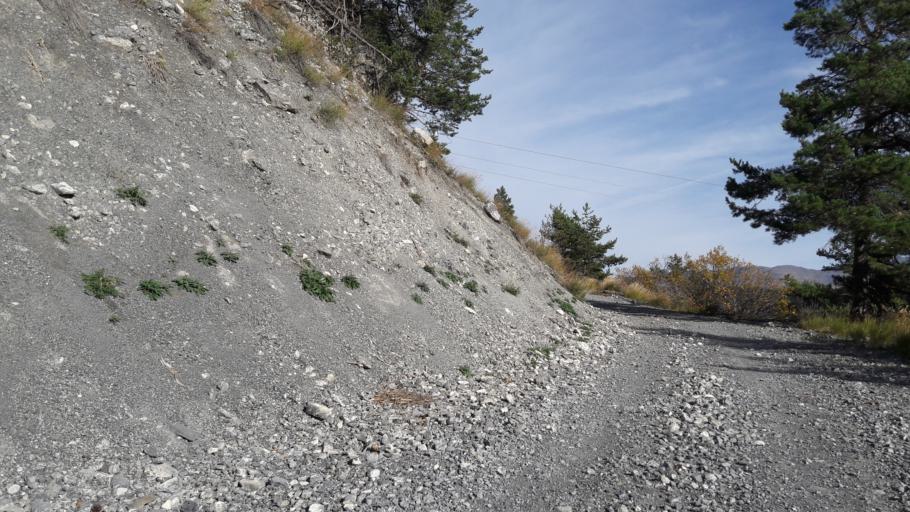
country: FR
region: Rhone-Alpes
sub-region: Departement de la Savoie
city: Valloire
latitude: 45.1891
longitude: 6.4294
